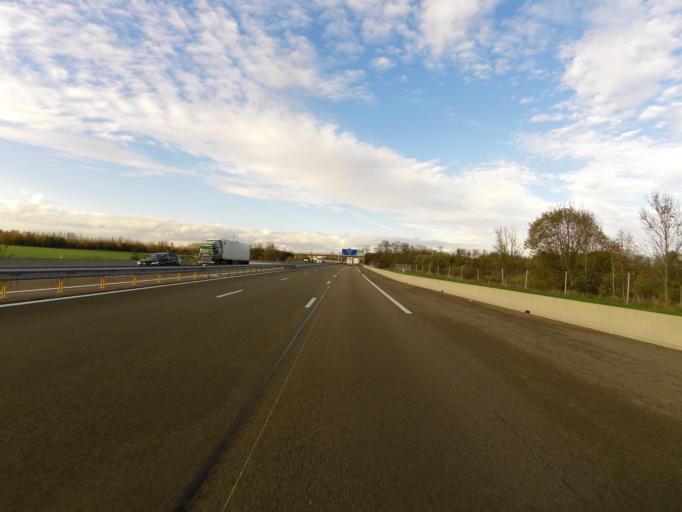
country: FR
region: Bourgogne
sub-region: Departement de la Cote-d'Or
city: Couternon
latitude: 47.3390
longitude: 5.1655
